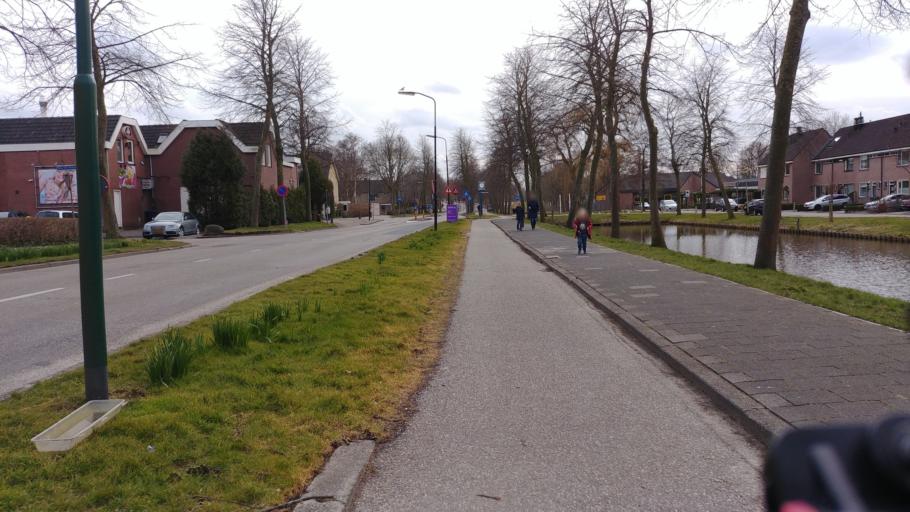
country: NL
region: Utrecht
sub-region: Gemeente De Ronde Venen
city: Mijdrecht
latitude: 52.2008
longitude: 4.8959
